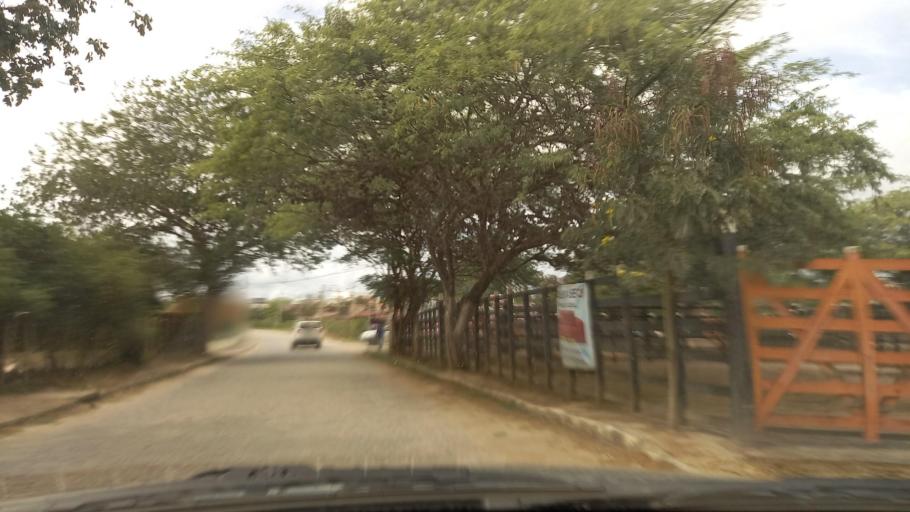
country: BR
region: Pernambuco
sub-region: Gravata
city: Gravata
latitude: -8.1932
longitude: -35.5773
